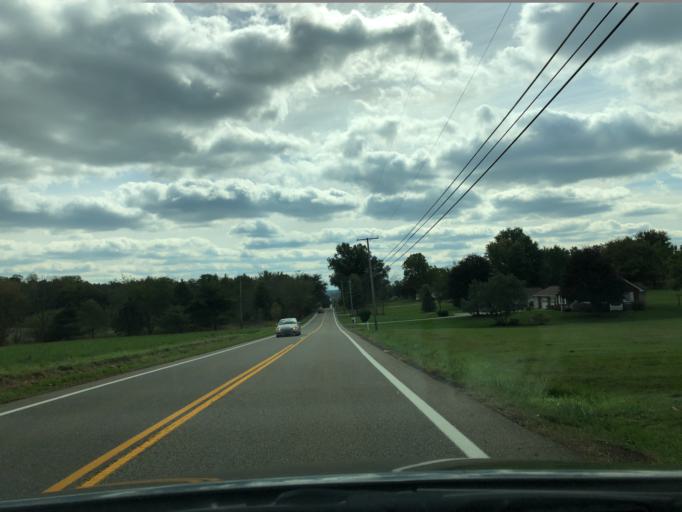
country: US
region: Ohio
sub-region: Stark County
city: Brewster
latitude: 40.7452
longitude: -81.5956
